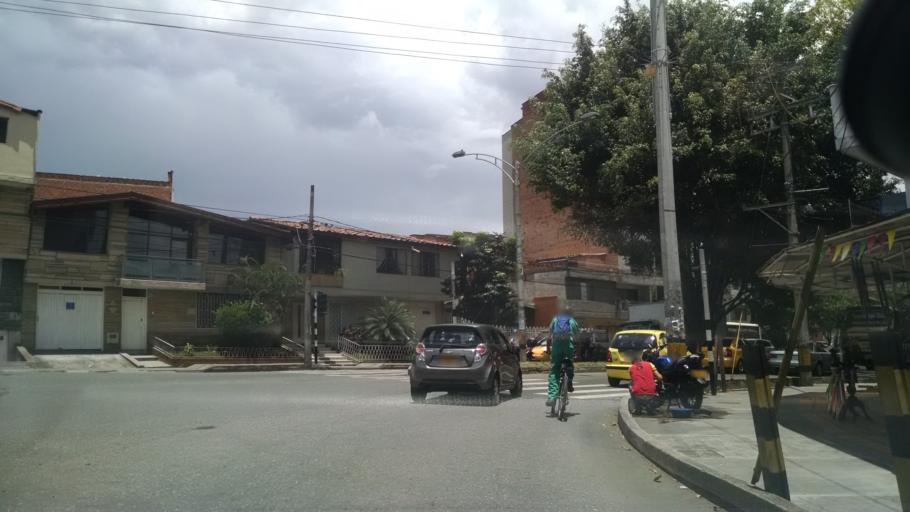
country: CO
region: Antioquia
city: Medellin
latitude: 6.2641
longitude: -75.6002
